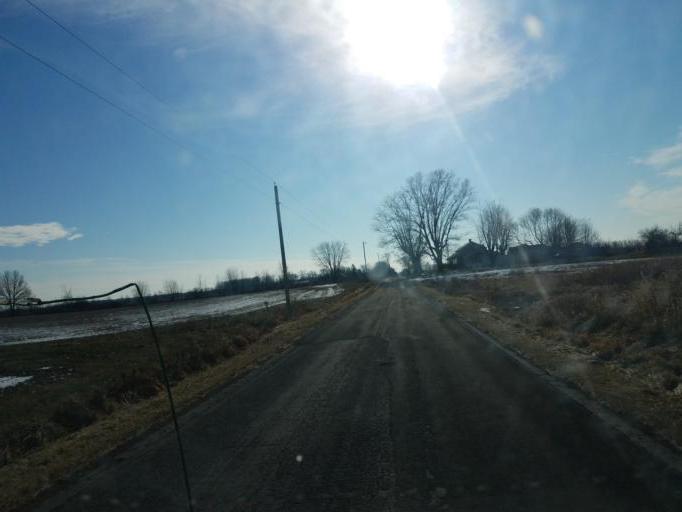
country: US
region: Ohio
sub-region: Morrow County
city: Cardington
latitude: 40.4763
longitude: -82.8696
